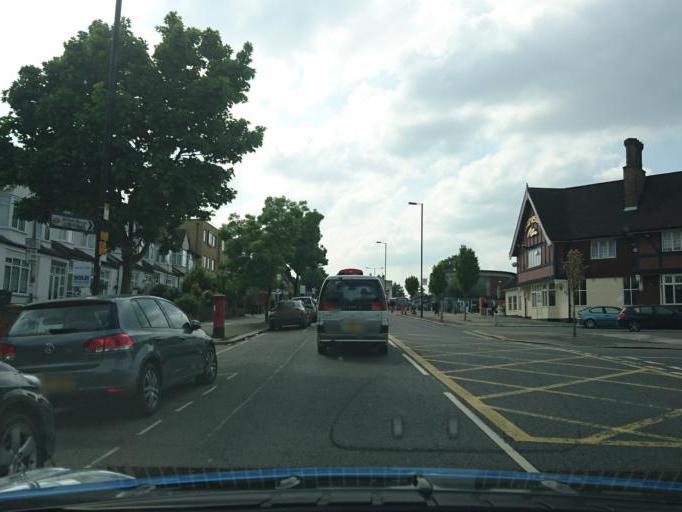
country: GB
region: England
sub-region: Greater London
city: Wood Green
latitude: 51.6159
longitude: -0.1315
